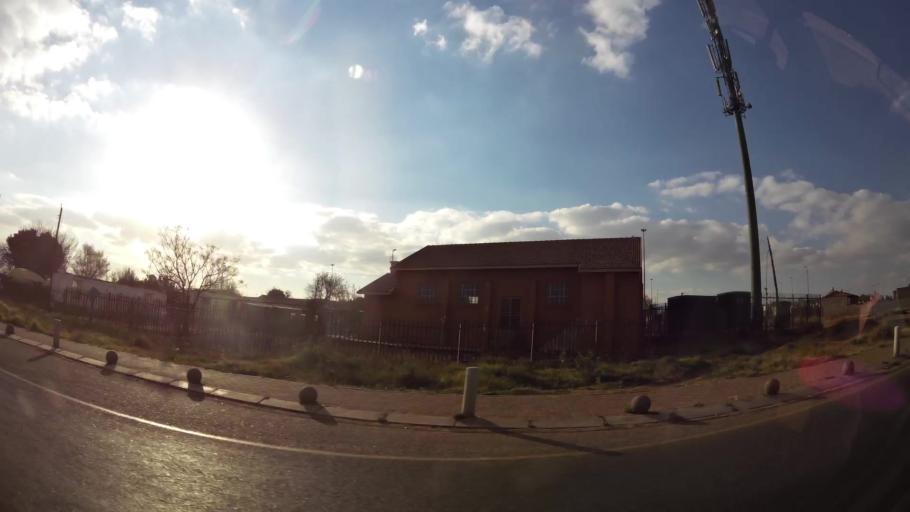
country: ZA
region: Gauteng
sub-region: West Rand District Municipality
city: Krugersdorp
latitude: -26.0817
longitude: 27.7586
